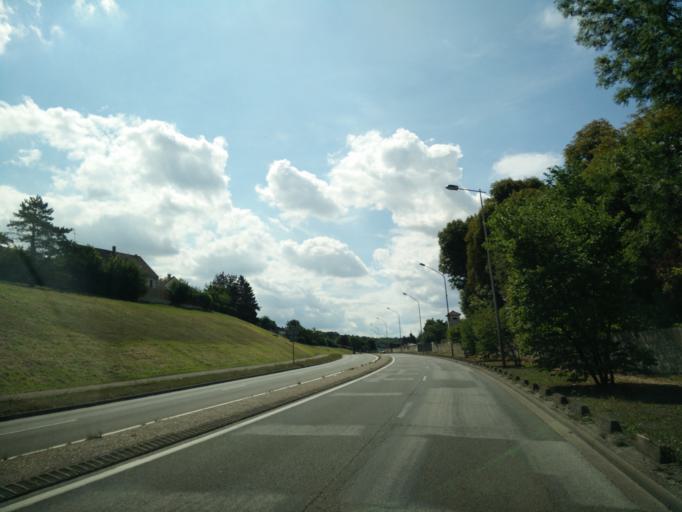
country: FR
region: Ile-de-France
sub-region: Departement des Yvelines
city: Mantes-la-Jolie
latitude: 48.9737
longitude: 1.7169
